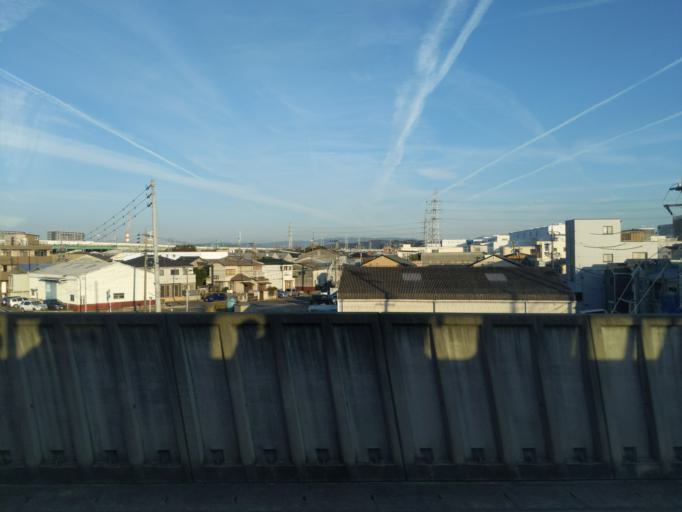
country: JP
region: Aichi
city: Kasugai
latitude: 35.2223
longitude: 136.9518
